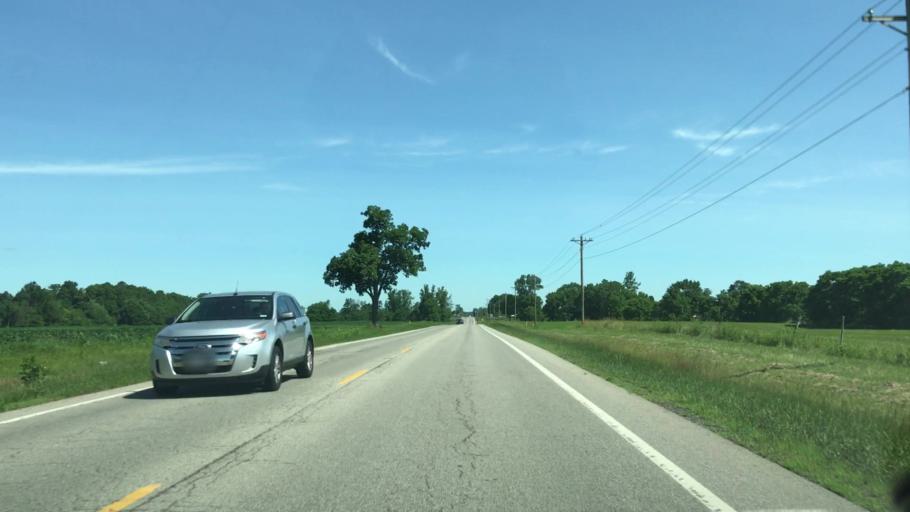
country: US
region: Ohio
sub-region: Huron County
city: Greenwich
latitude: 41.0325
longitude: -82.4854
